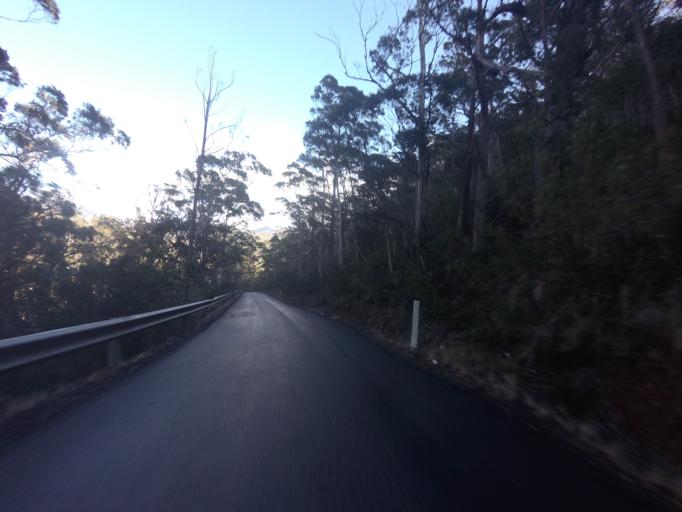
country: AU
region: Tasmania
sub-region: Glenorchy
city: Berriedale
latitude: -42.8190
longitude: 147.1892
